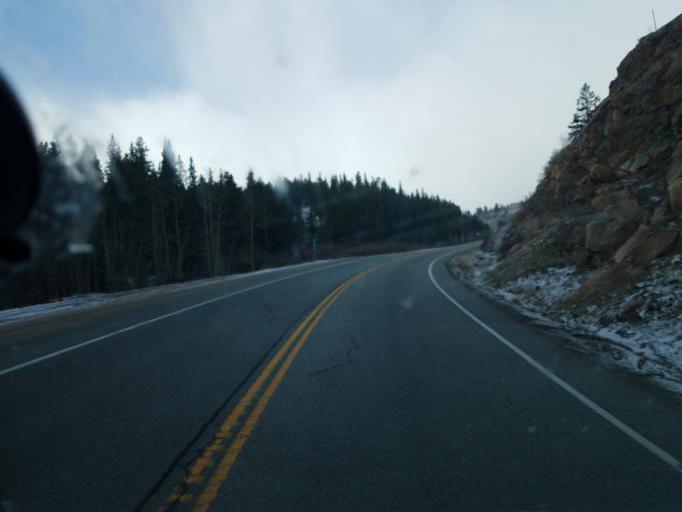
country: US
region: Colorado
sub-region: Clear Creek County
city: Georgetown
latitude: 39.4427
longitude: -105.7437
